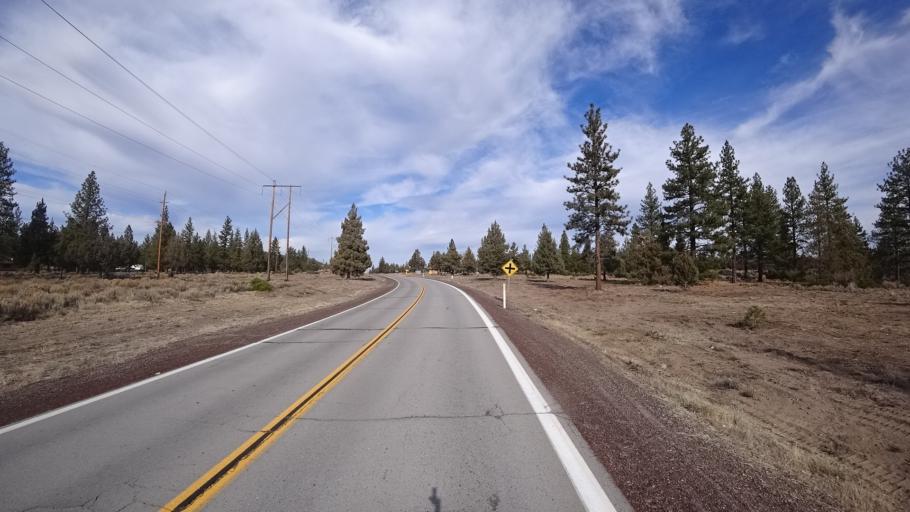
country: US
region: California
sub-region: Siskiyou County
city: Weed
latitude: 41.5262
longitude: -122.3649
